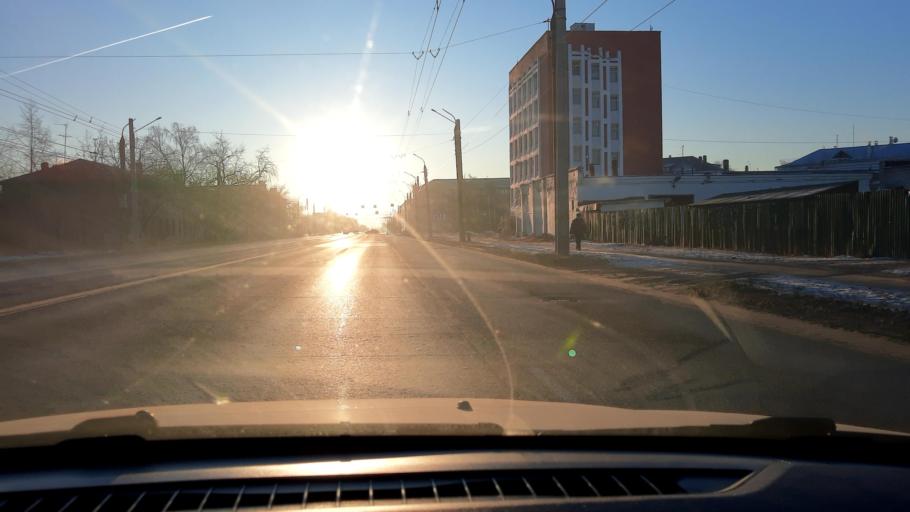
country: RU
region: Nizjnij Novgorod
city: Dzerzhinsk
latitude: 56.2465
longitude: 43.4759
